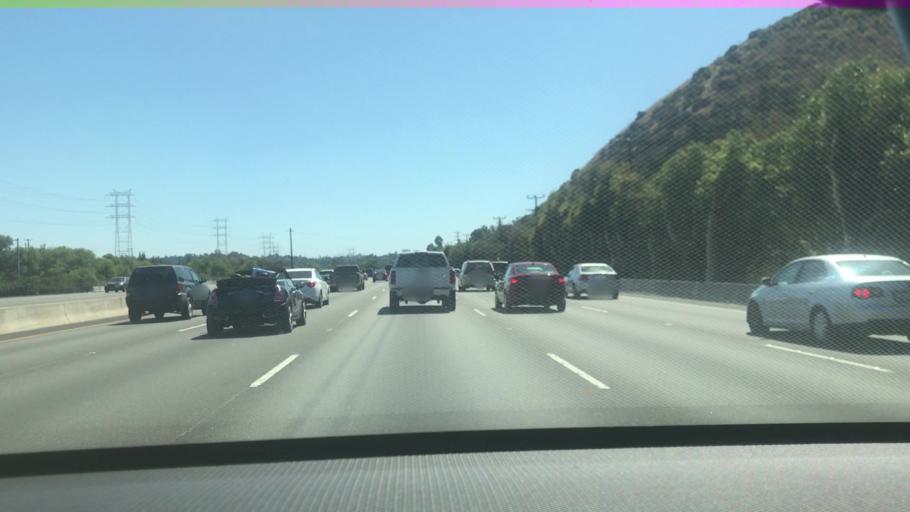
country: US
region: California
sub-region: Los Angeles County
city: Glendale
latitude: 34.1342
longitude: -118.2757
